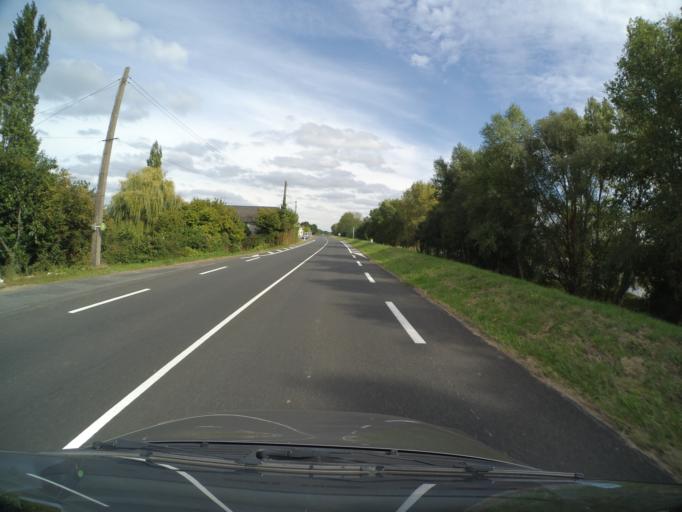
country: FR
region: Centre
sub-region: Departement d'Indre-et-Loire
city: Huismes
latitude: 47.2644
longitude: 0.2741
